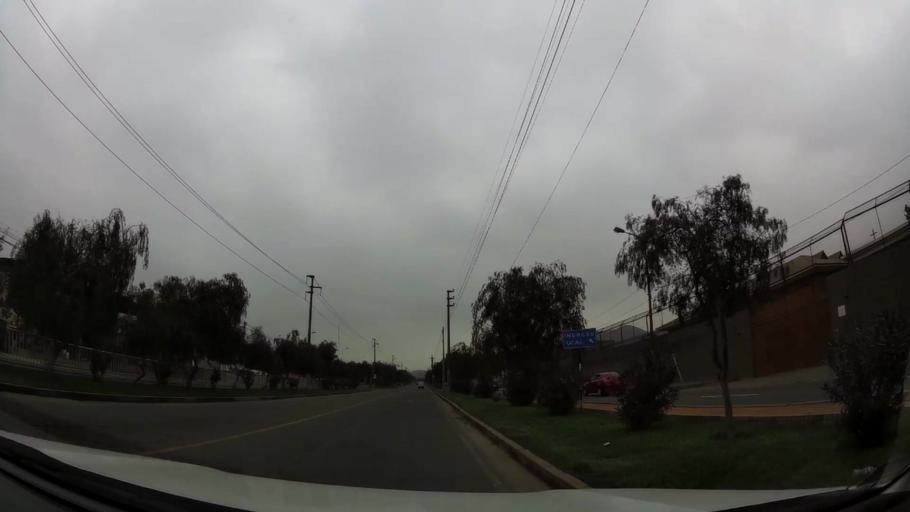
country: PE
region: Lima
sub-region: Lima
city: La Molina
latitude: -12.0863
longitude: -76.9081
